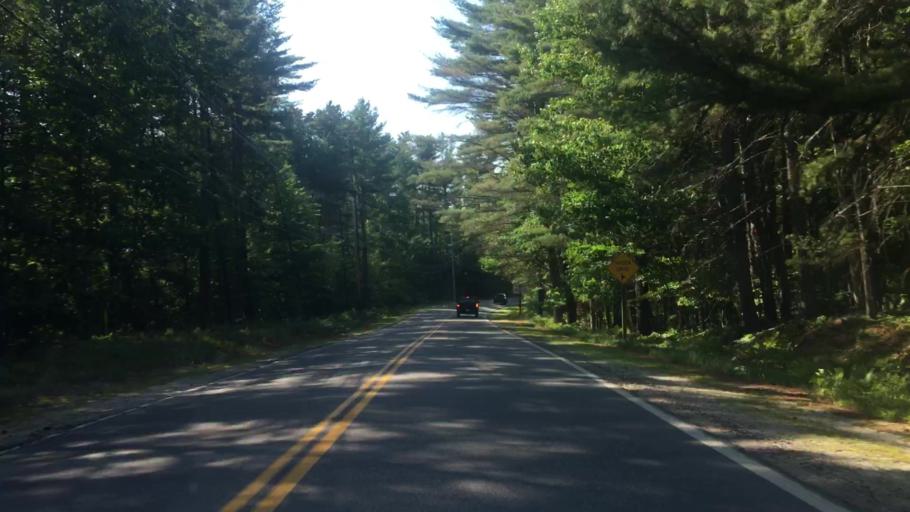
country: US
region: Maine
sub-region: York County
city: Hollis Center
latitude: 43.6901
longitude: -70.5949
